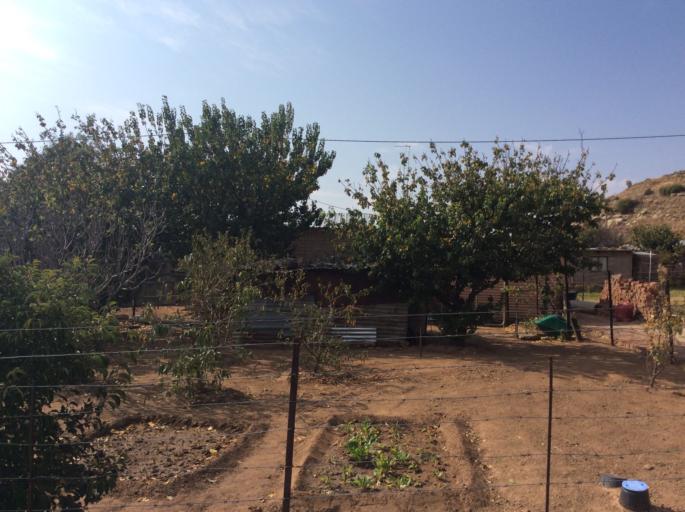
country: ZA
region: Orange Free State
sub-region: Xhariep District Municipality
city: Dewetsdorp
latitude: -29.5857
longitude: 26.6708
